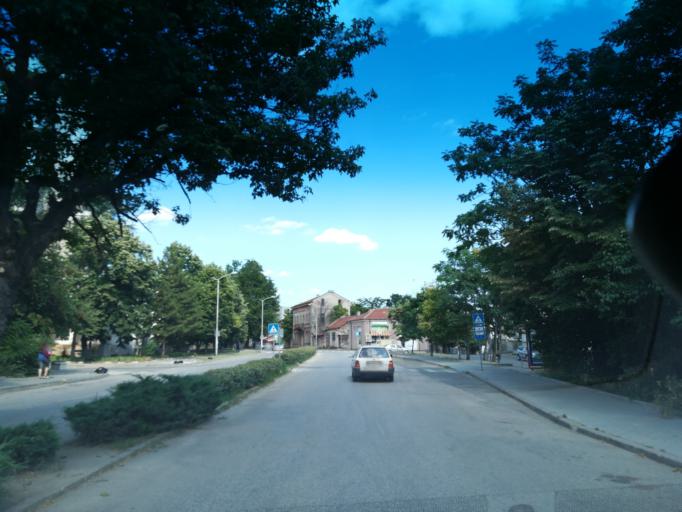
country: BG
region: Stara Zagora
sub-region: Obshtina Chirpan
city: Chirpan
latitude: 42.1983
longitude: 25.3295
